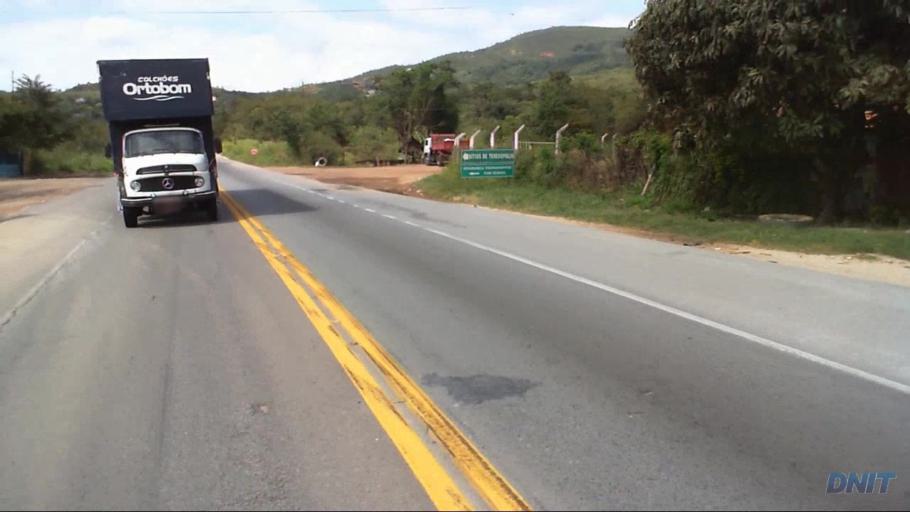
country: BR
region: Minas Gerais
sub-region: Santa Luzia
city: Santa Luzia
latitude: -19.8161
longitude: -43.8050
